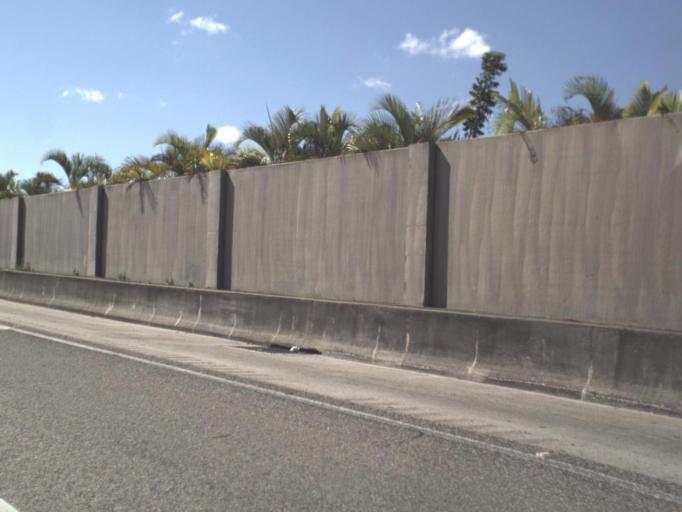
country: US
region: Florida
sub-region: Miami-Dade County
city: Westwood Lake
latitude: 25.7184
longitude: -80.3842
